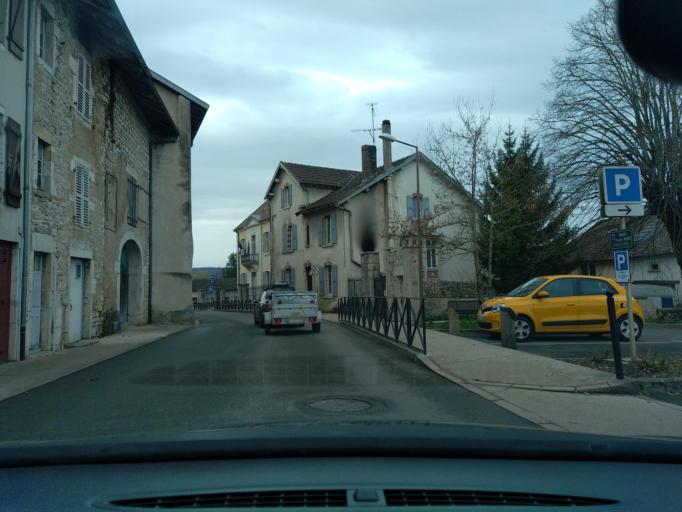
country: FR
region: Franche-Comte
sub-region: Departement du Jura
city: Arinthod
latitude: 46.3937
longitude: 5.5652
